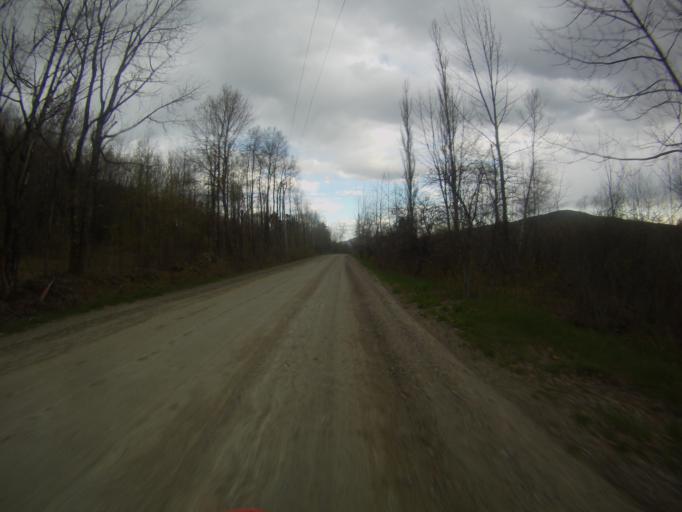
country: US
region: Vermont
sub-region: Addison County
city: Bristol
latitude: 44.0445
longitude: -73.0145
